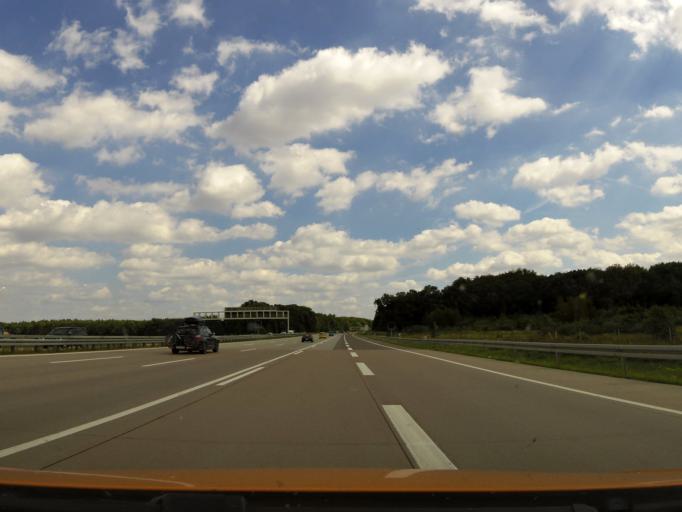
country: DE
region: Brandenburg
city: Ahrensfelde
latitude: 52.6113
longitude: 13.5779
